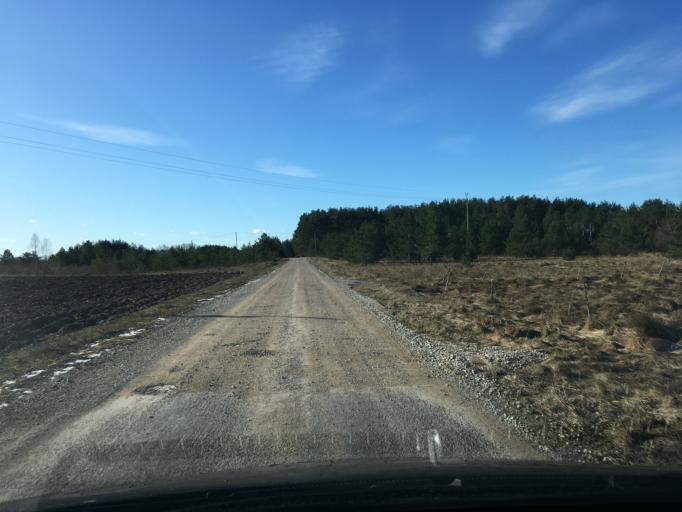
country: EE
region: Laeaene
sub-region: Lihula vald
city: Lihula
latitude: 58.5821
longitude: 23.7046
